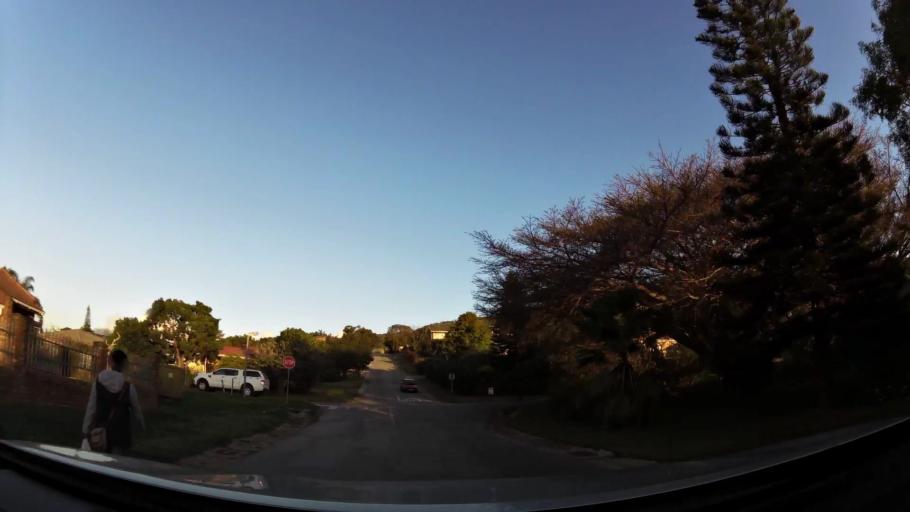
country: ZA
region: Western Cape
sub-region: Eden District Municipality
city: Knysna
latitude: -34.0206
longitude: 22.8123
